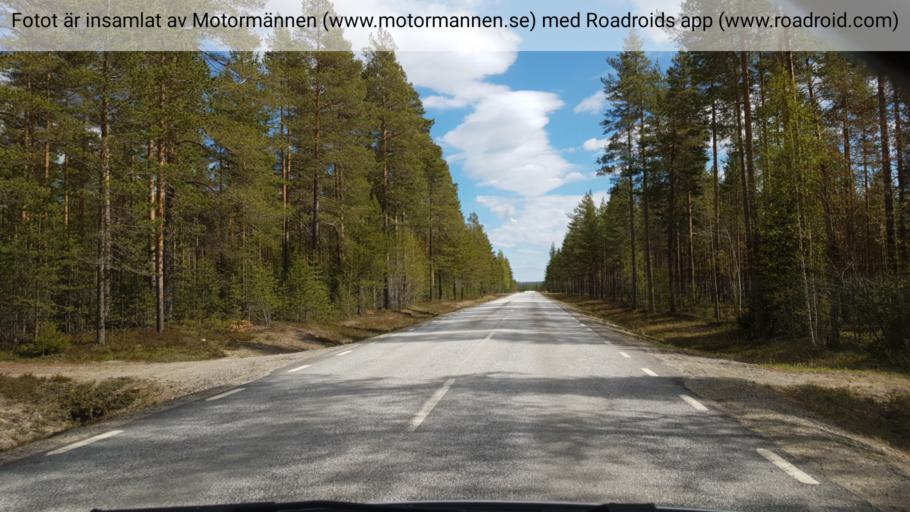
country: SE
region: Vaesterbotten
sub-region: Vindelns Kommun
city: Vindeln
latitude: 64.2131
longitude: 19.3974
